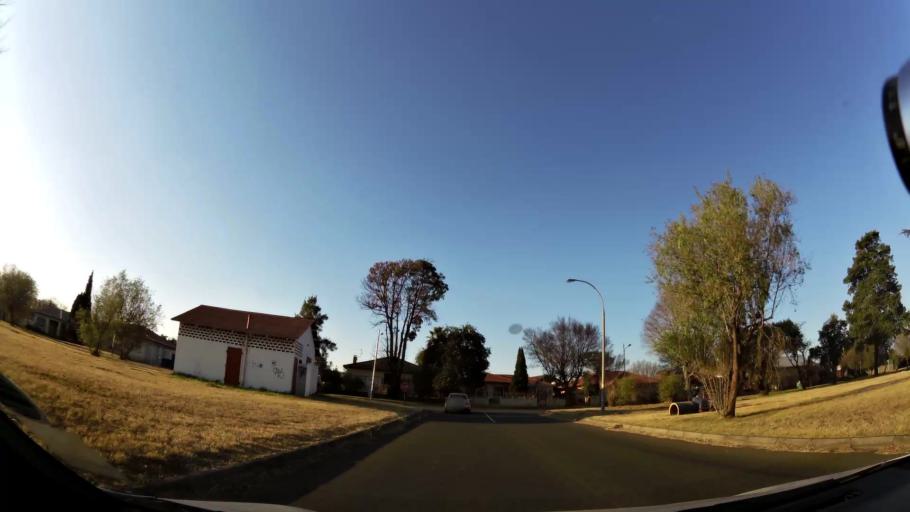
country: ZA
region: Gauteng
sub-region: Ekurhuleni Metropolitan Municipality
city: Germiston
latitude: -26.2641
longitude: 28.1307
